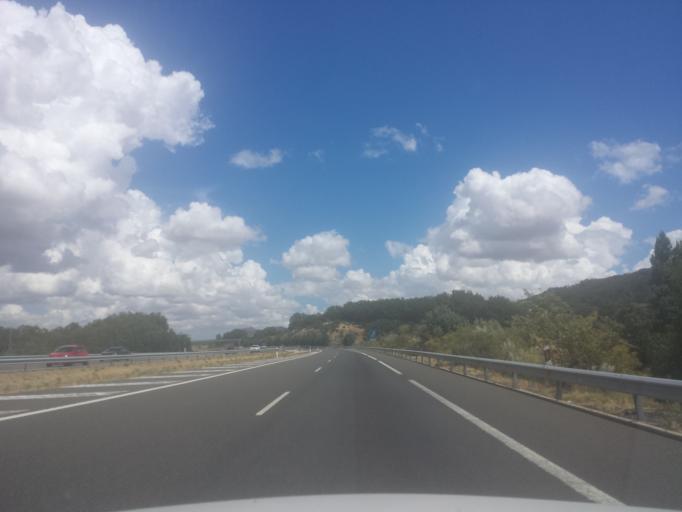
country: ES
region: Castille and Leon
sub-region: Provincia de Salamanca
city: Cantagallo
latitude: 40.3687
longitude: -5.8285
